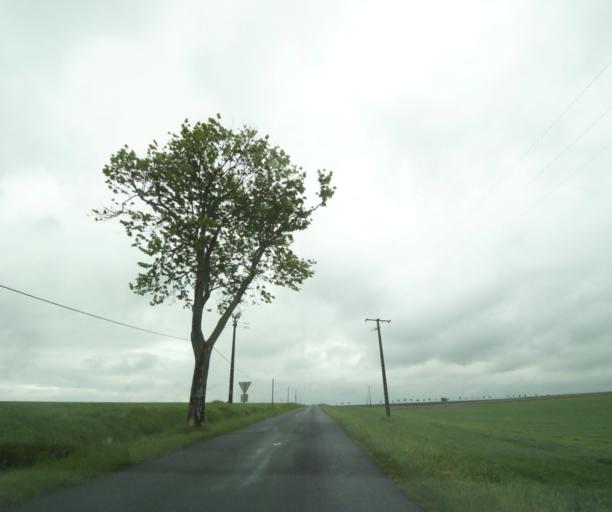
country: FR
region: Poitou-Charentes
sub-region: Departement de la Charente-Maritime
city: Perignac
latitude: 45.6483
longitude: -0.5236
